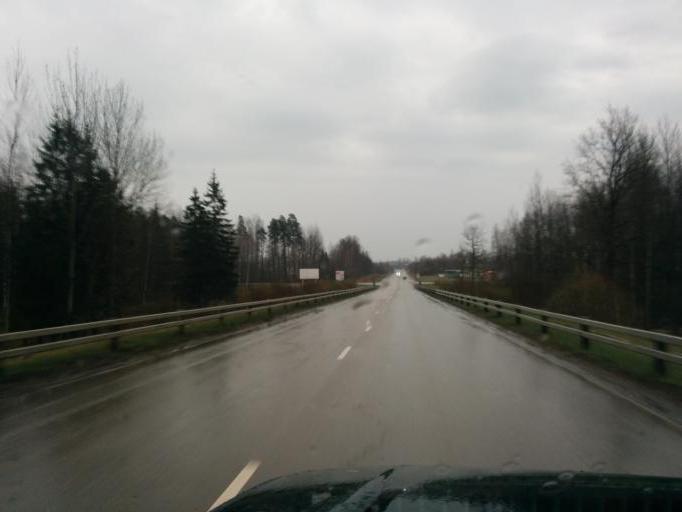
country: LV
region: Ozolnieku
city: Ozolnieki
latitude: 56.6620
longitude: 23.7822
